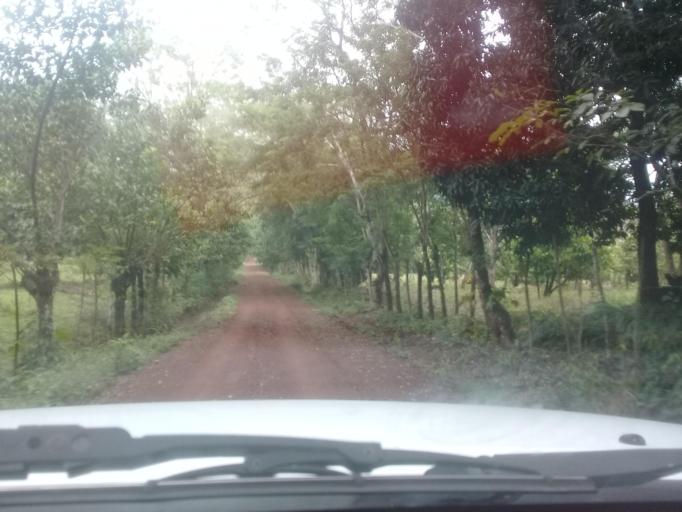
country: MX
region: Veracruz
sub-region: San Andres Tuxtla
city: Cerro las Iguanas
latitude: 18.4015
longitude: -95.2034
